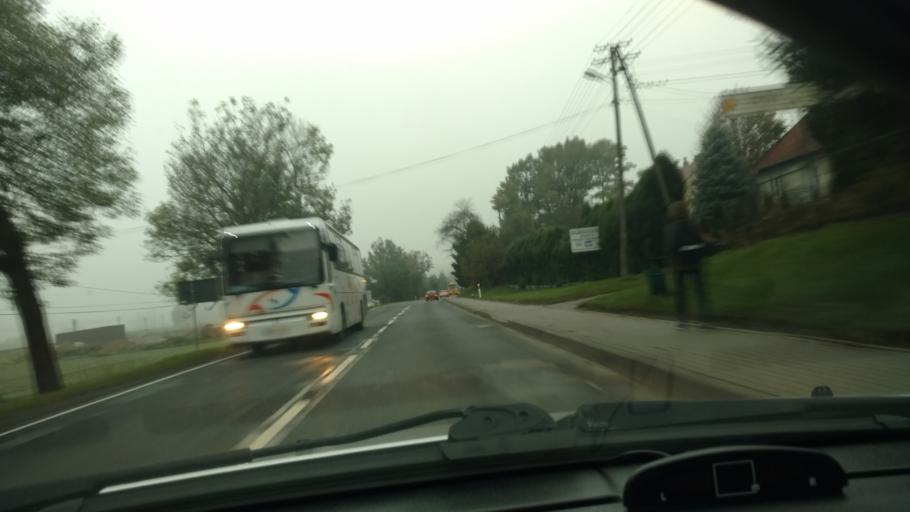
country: PL
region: Subcarpathian Voivodeship
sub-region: Powiat strzyzowski
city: Wisniowa
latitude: 49.8689
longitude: 21.6592
